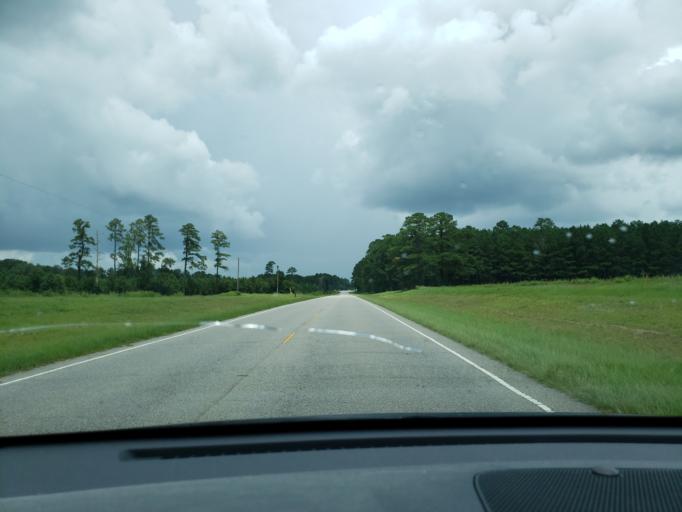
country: US
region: North Carolina
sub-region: Bladen County
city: Bladenboro
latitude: 34.4780
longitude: -78.6666
